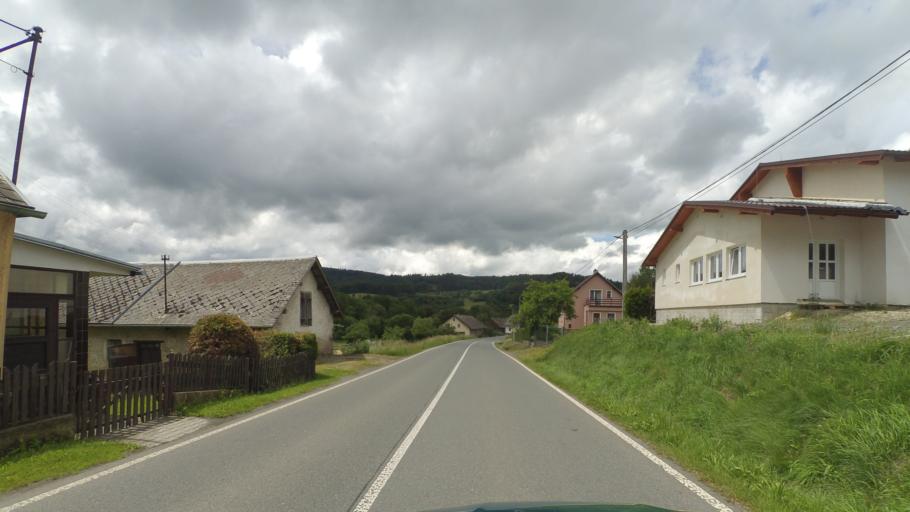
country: CZ
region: Plzensky
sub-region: Okres Klatovy
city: Nyrsko
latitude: 49.2746
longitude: 13.1559
